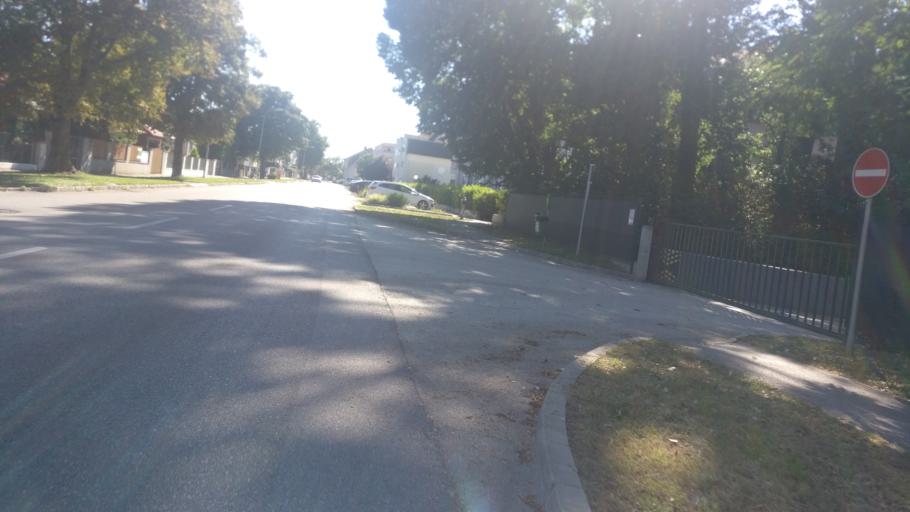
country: AT
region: Lower Austria
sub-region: Politischer Bezirk Baden
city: Mitterndorf an der Fischa
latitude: 47.9647
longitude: 16.4377
